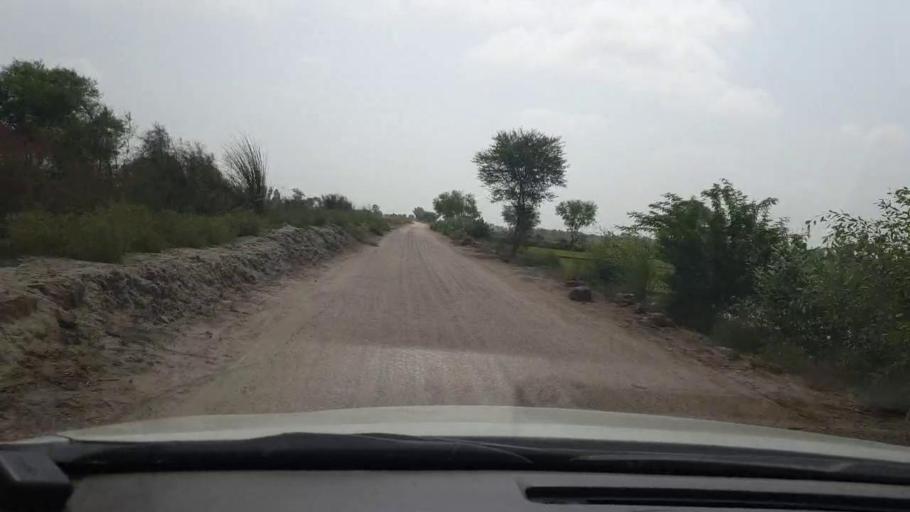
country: PK
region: Sindh
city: Shikarpur
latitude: 28.0104
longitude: 68.5640
